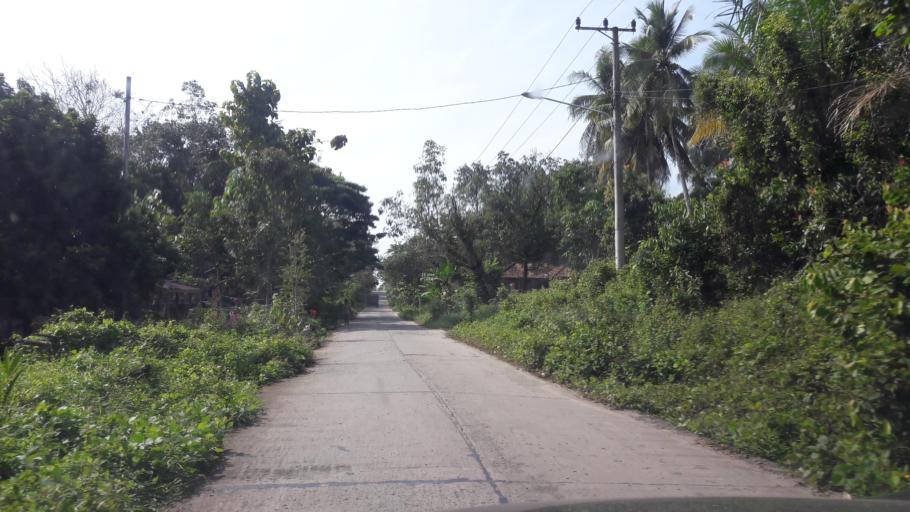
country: ID
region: South Sumatra
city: Gunungmenang
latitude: -3.3314
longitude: 104.0605
